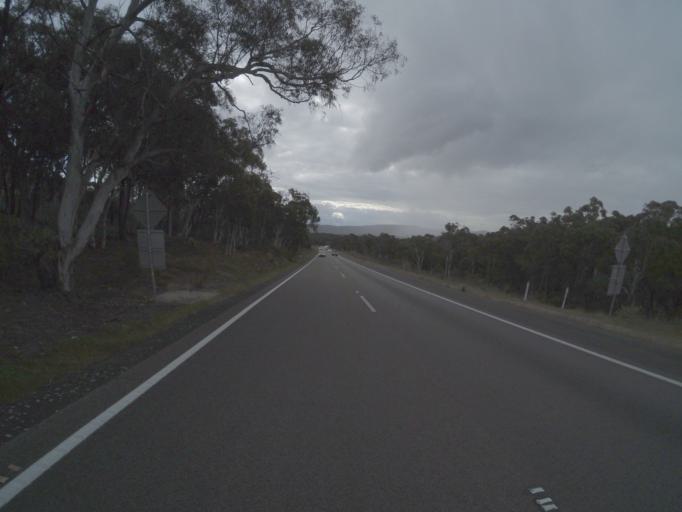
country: AU
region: New South Wales
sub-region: Goulburn Mulwaree
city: Goulburn
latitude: -34.7413
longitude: 149.8392
